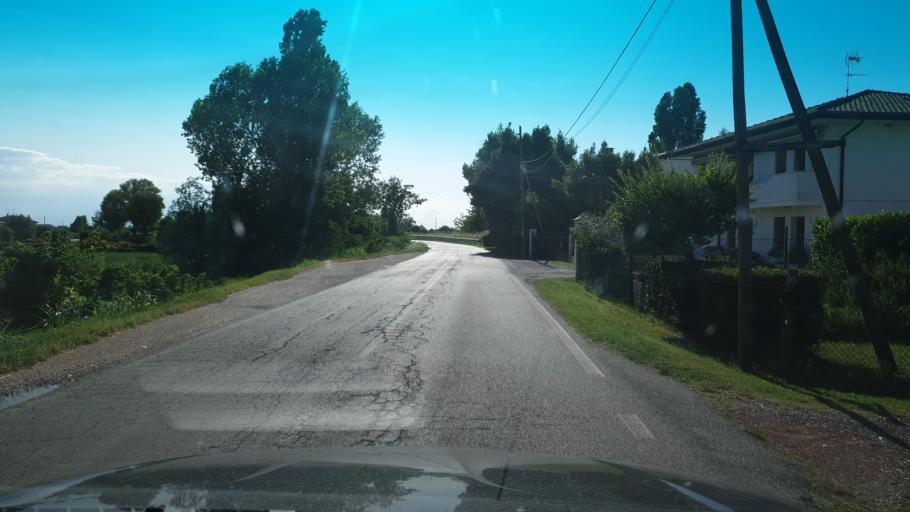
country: IT
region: Veneto
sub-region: Provincia di Rovigo
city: Grignano Polesine
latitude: 45.0727
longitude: 11.7405
